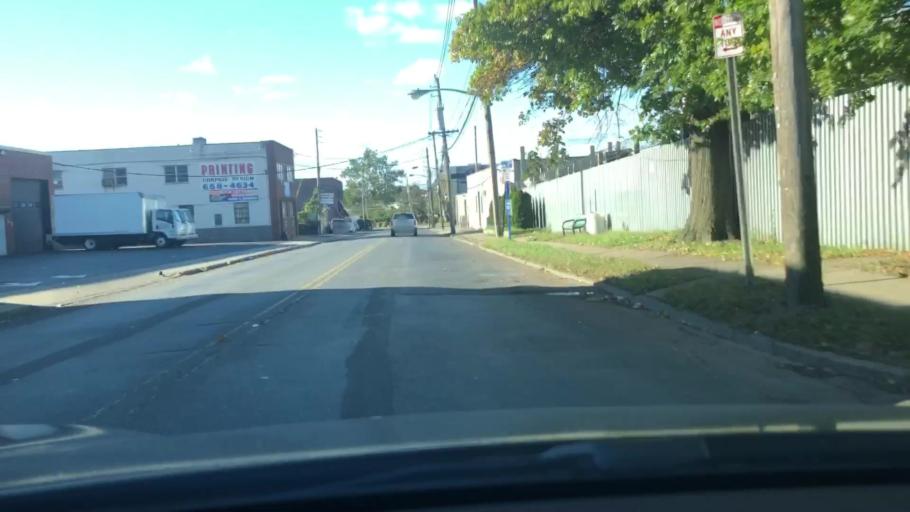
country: US
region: New York
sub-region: Westchester County
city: Pelham Manor
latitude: 40.8991
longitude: -73.8214
